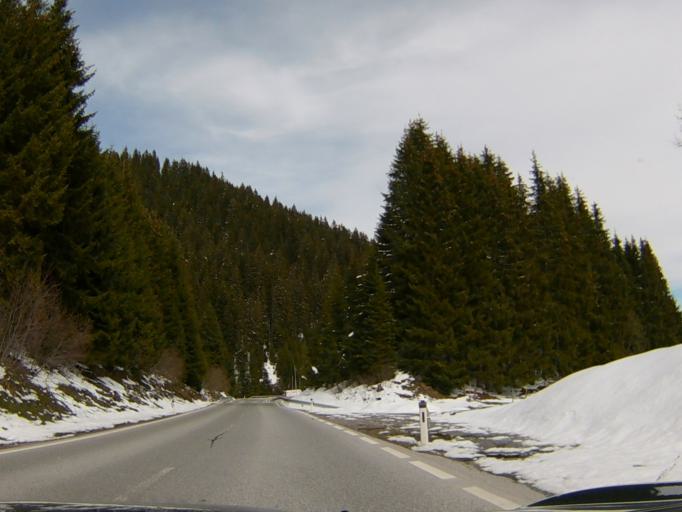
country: AT
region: Salzburg
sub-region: Politischer Bezirk Zell am See
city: Krimml
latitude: 47.2430
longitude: 12.0961
